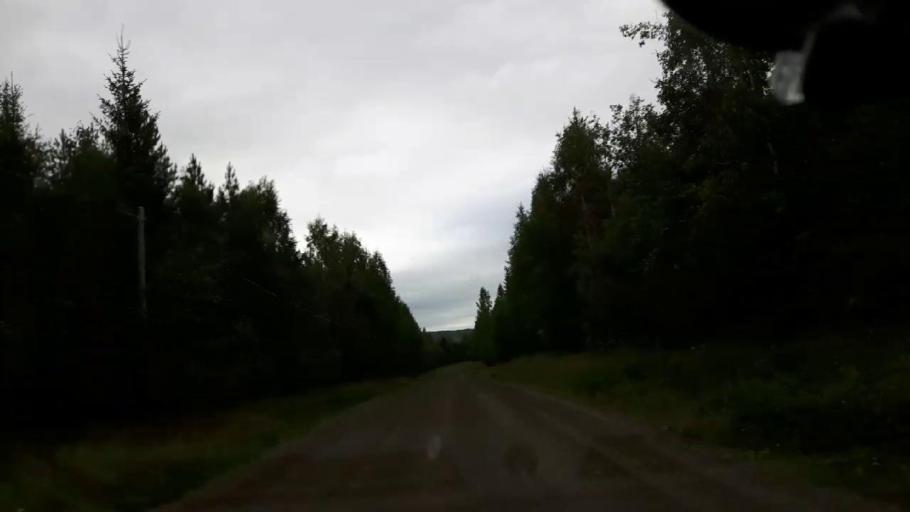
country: SE
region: Jaemtland
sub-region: Braecke Kommun
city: Braecke
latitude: 62.9047
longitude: 15.5946
